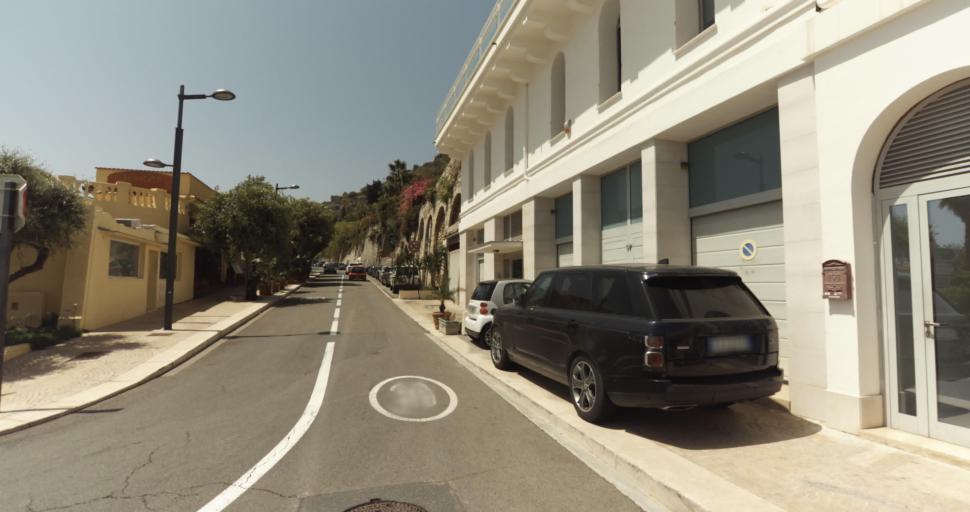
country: FR
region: Provence-Alpes-Cote d'Azur
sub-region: Departement des Alpes-Maritimes
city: Menton
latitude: 43.7861
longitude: 7.5282
